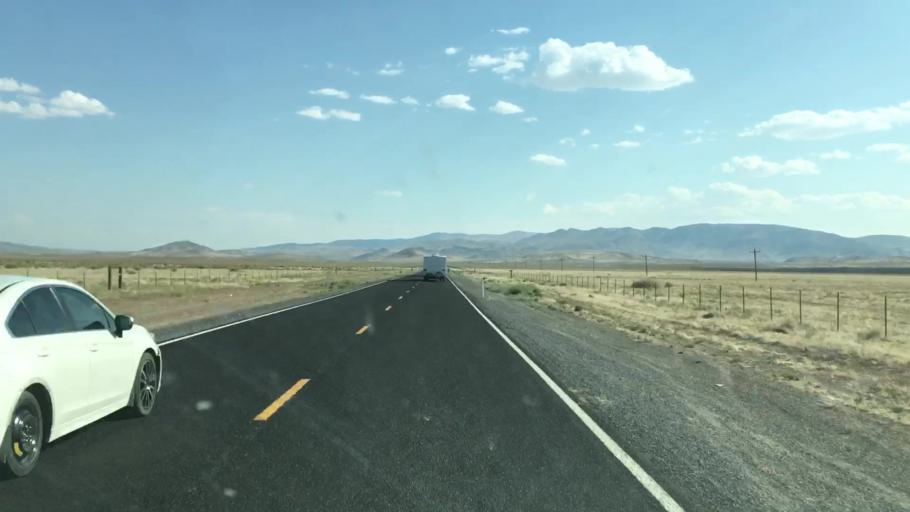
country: US
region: Nevada
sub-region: Lyon County
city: Fernley
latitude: 39.6825
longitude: -119.3346
